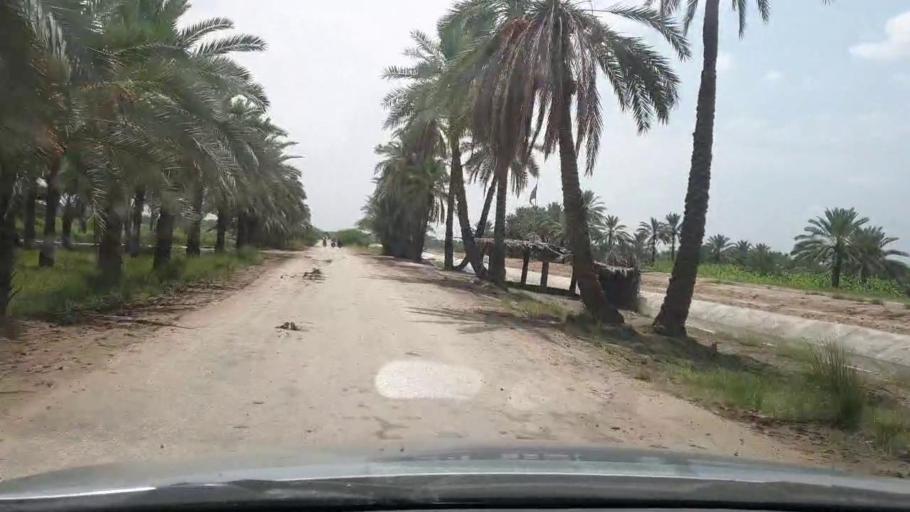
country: PK
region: Sindh
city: Khairpur
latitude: 27.4265
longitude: 68.7809
